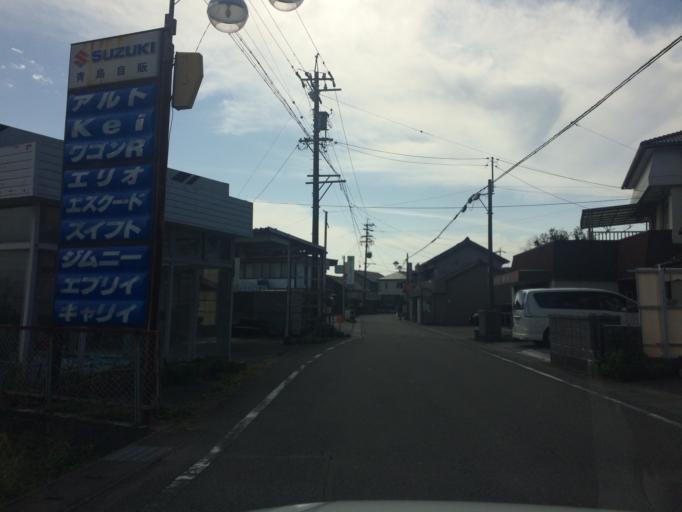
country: JP
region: Shizuoka
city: Yaizu
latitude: 34.7953
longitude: 138.2966
